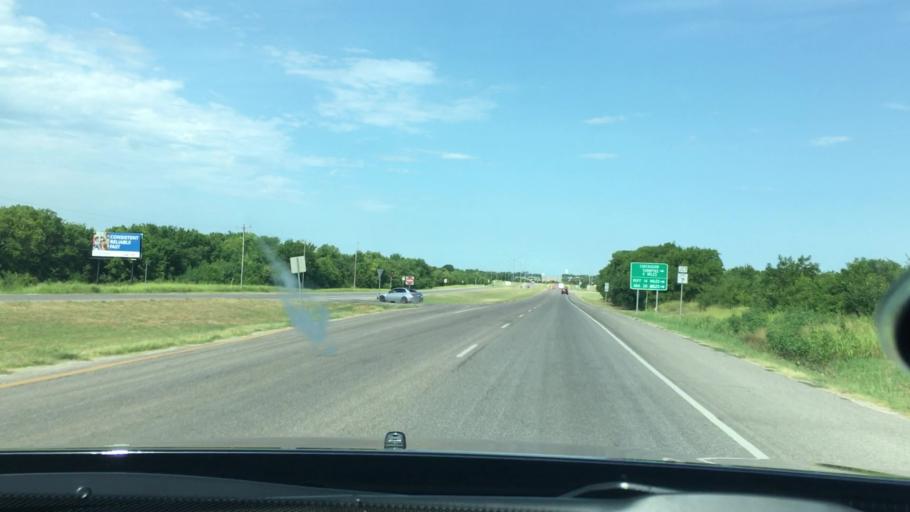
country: US
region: Oklahoma
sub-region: Murray County
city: Sulphur
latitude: 34.5064
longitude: -97.0076
